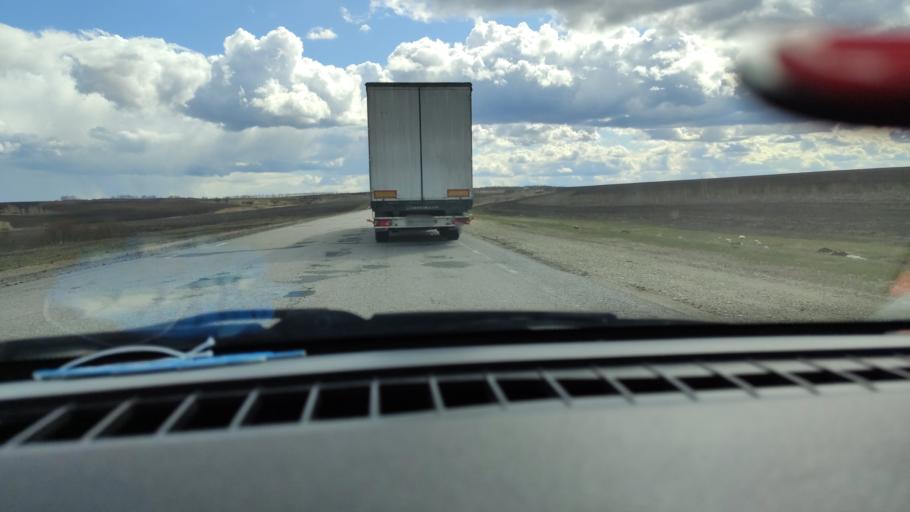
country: RU
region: Samara
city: Varlamovo
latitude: 53.0113
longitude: 48.3321
